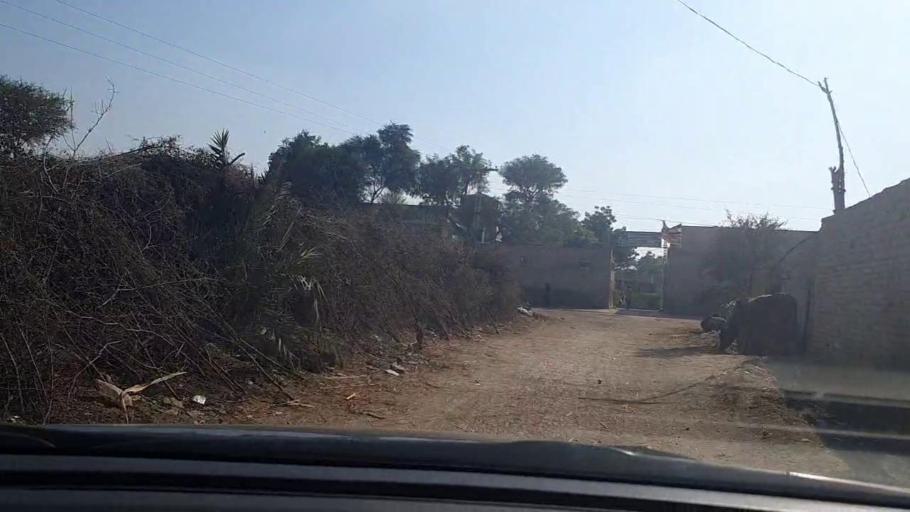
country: PK
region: Sindh
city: Sann
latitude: 26.2700
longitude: 68.0707
